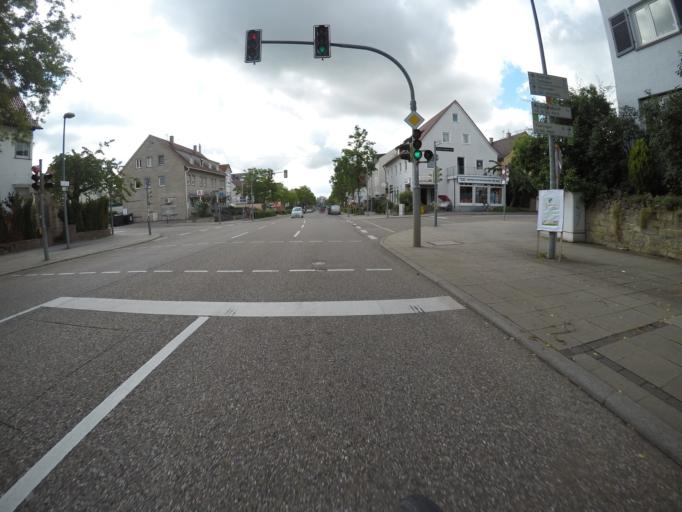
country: DE
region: Baden-Wuerttemberg
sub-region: Regierungsbezirk Stuttgart
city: Stuttgart-Ost
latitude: 48.7466
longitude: 9.2098
